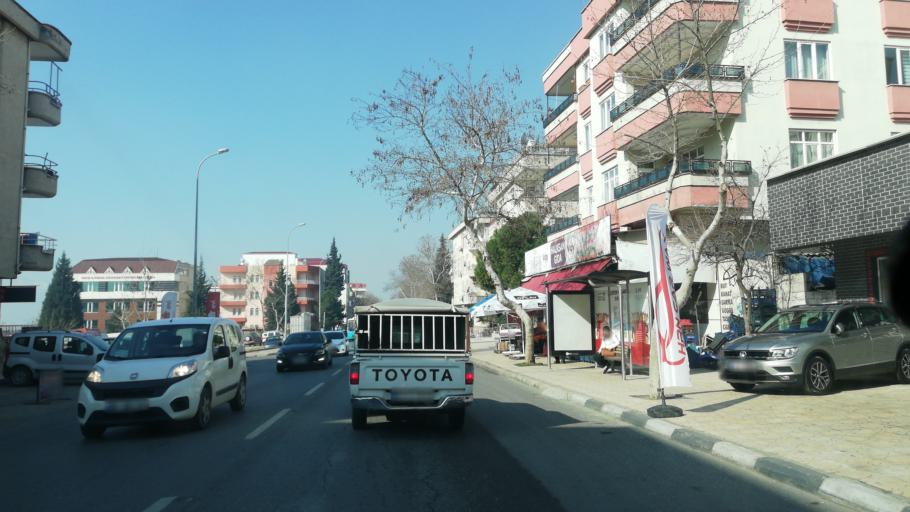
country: TR
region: Kahramanmaras
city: Kahramanmaras
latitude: 37.5719
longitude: 36.9347
